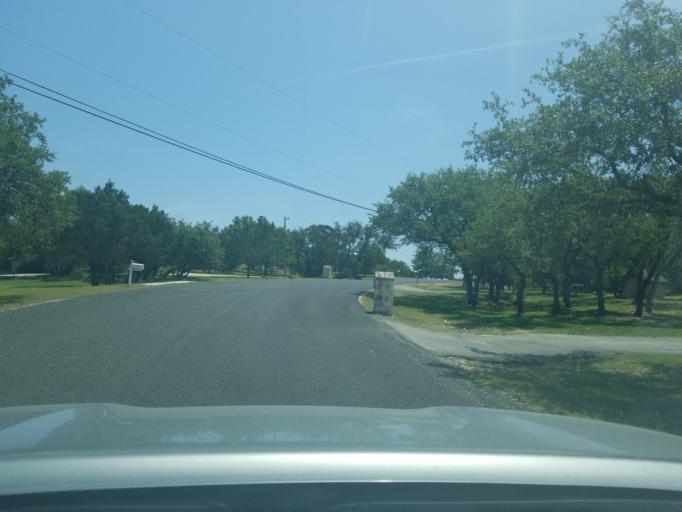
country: US
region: Texas
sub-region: Bexar County
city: Timberwood Park
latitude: 29.6685
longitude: -98.5133
